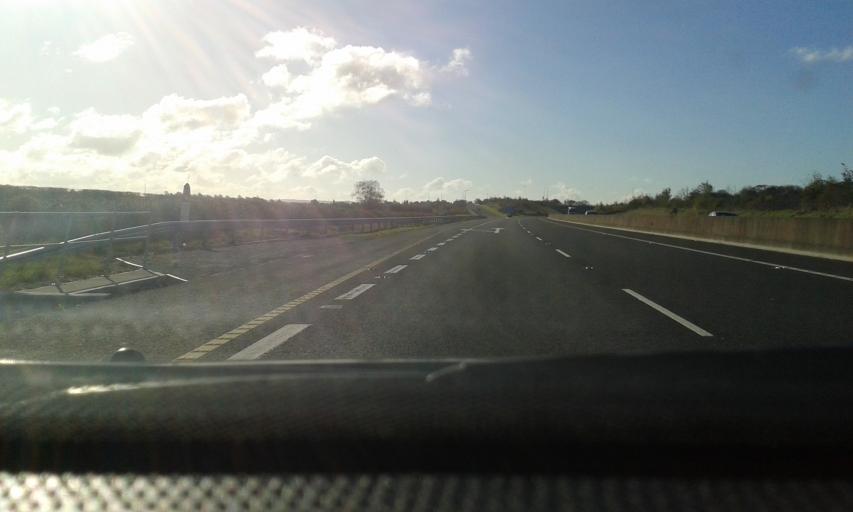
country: IE
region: Leinster
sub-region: Laois
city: Rathdowney
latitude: 52.7352
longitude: -7.5798
